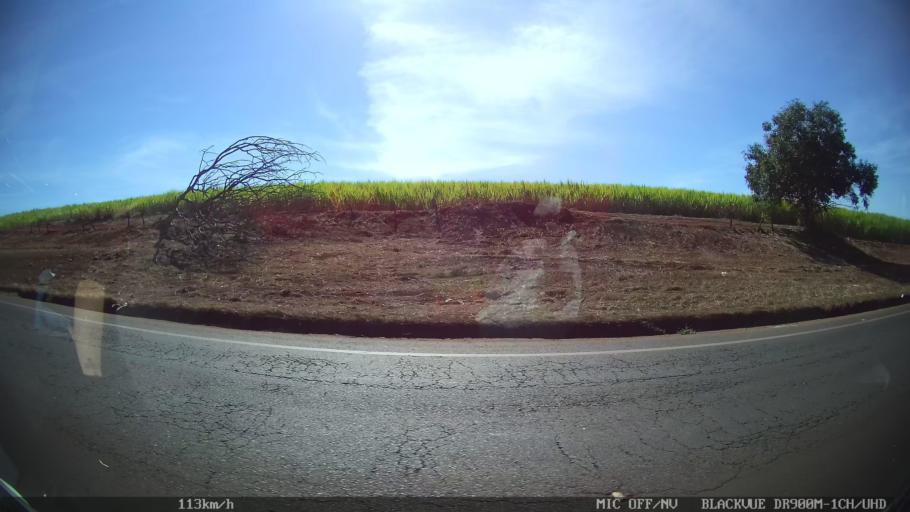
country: BR
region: Sao Paulo
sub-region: Ipua
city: Ipua
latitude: -20.4934
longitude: -48.0267
